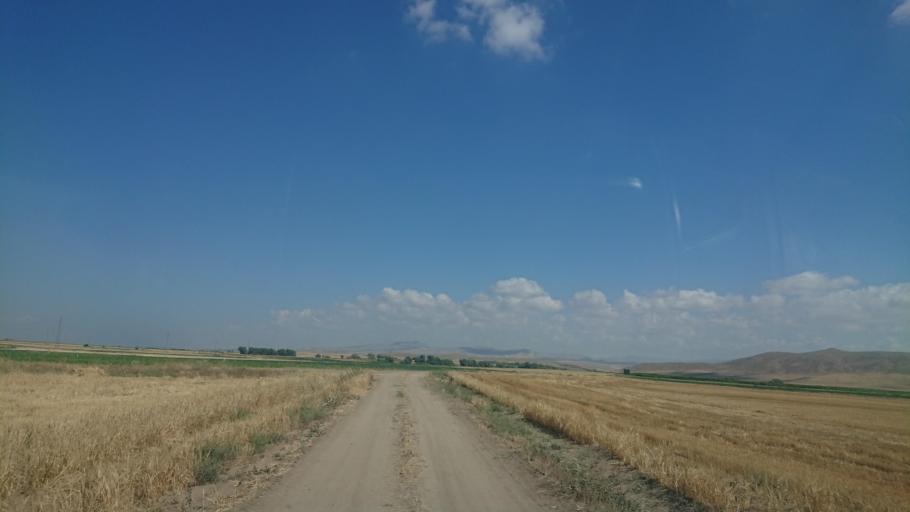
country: TR
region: Aksaray
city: Sariyahsi
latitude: 38.9876
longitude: 33.9026
